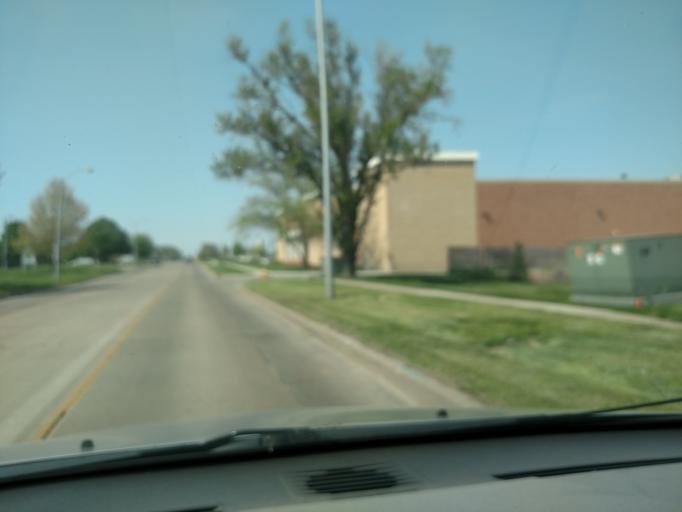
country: US
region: Iowa
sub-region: Polk County
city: Clive
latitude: 41.5969
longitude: -93.7616
